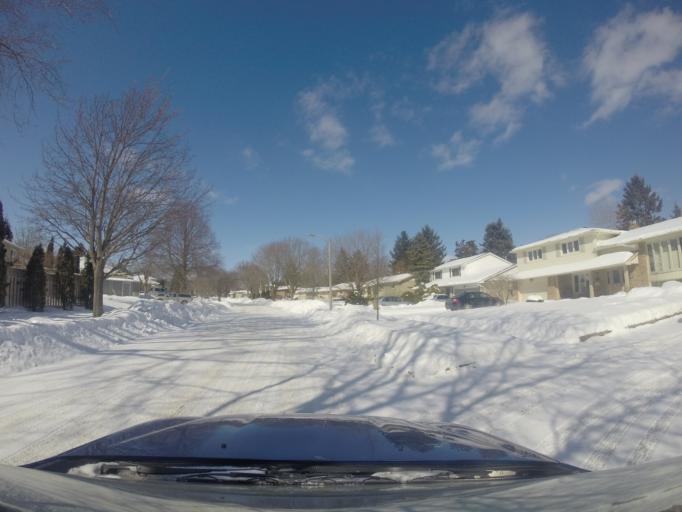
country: CA
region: Ontario
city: Burlington
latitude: 43.3426
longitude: -79.7672
